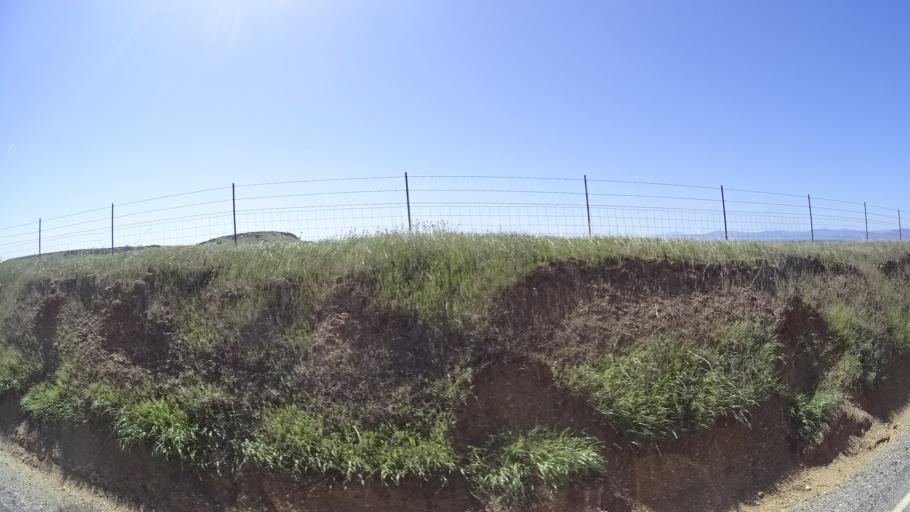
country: US
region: California
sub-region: Glenn County
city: Orland
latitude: 39.8286
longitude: -122.3592
